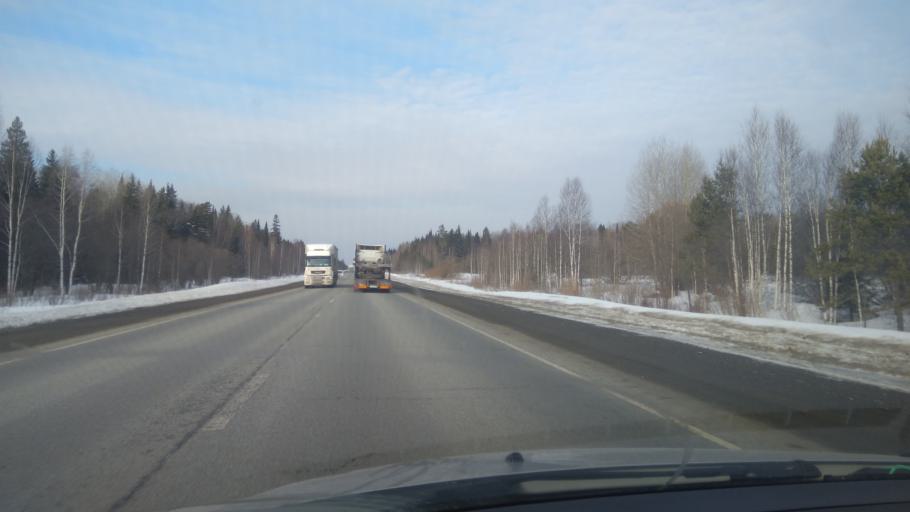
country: RU
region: Sverdlovsk
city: Druzhinino
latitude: 56.7973
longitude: 59.4485
